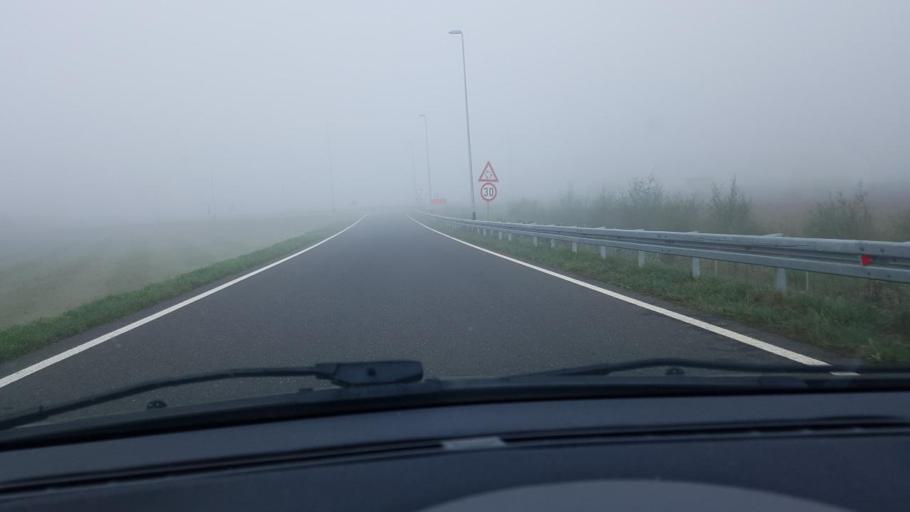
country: HR
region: Krapinsko-Zagorska
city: Bedekovcina
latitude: 46.0336
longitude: 15.9962
